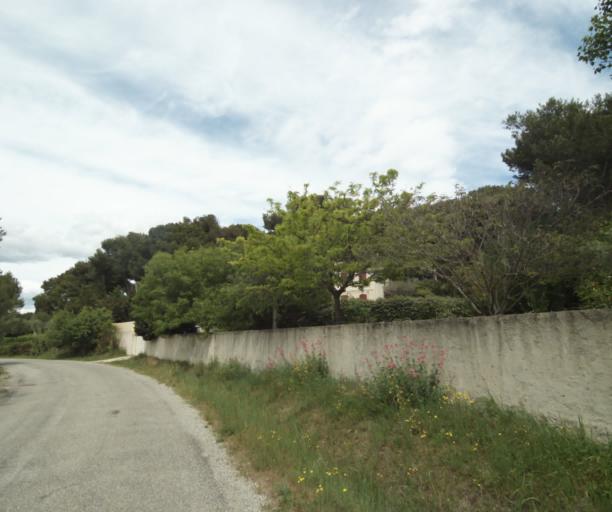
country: FR
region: Provence-Alpes-Cote d'Azur
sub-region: Departement des Bouches-du-Rhone
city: Rognac
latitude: 43.4790
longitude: 5.2406
